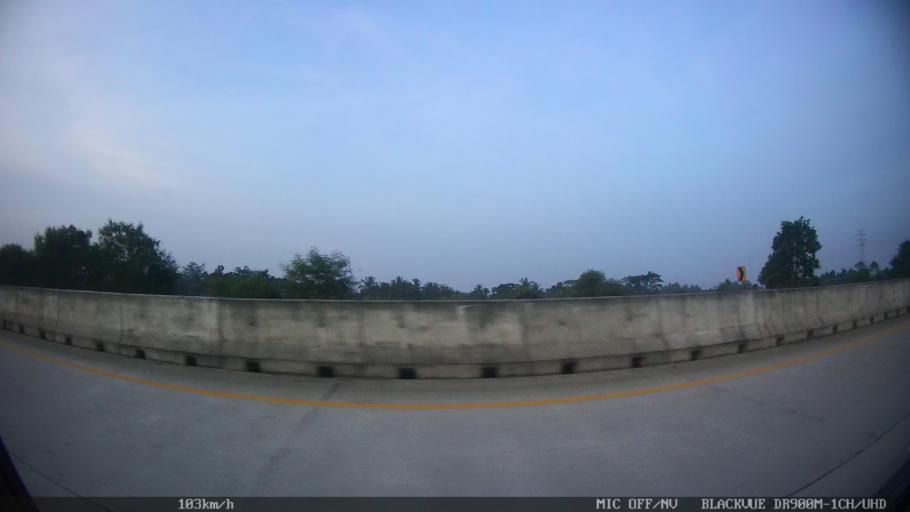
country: ID
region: Lampung
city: Pasuruan
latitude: -5.7182
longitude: 105.6604
